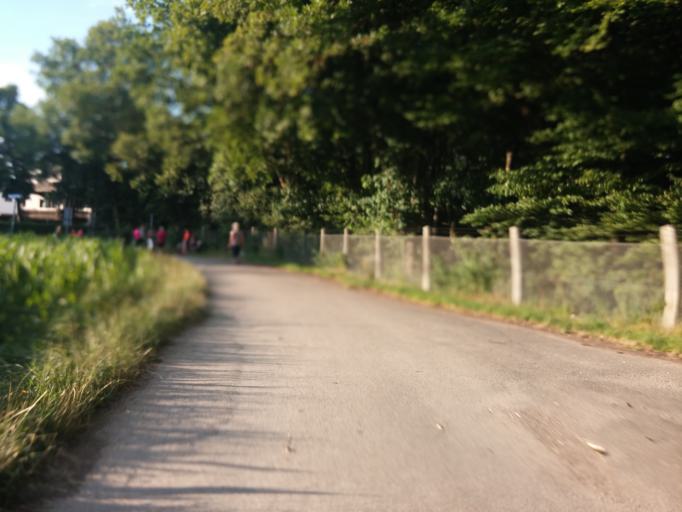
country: DE
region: Bavaria
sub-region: Upper Bavaria
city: Haar
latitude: 48.1083
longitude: 11.6857
